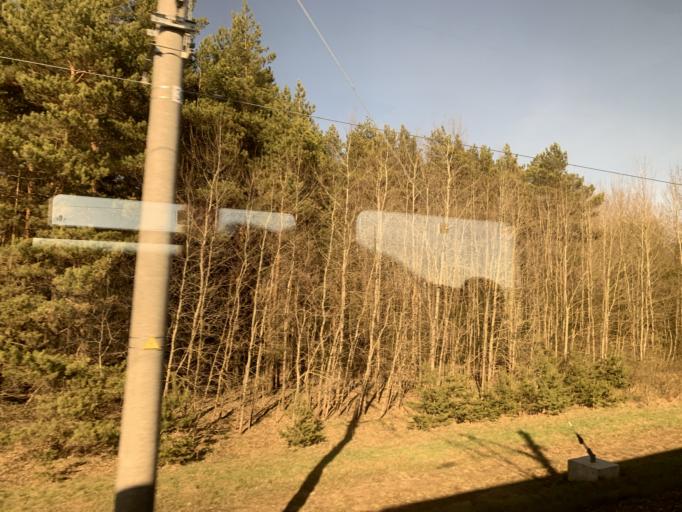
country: BY
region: Grodnenskaya
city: Astravyets
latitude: 54.5758
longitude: 25.9413
